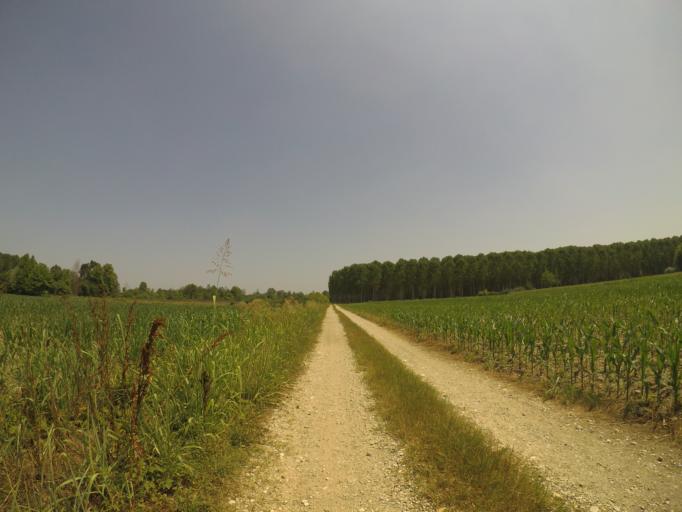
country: IT
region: Friuli Venezia Giulia
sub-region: Provincia di Udine
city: Bertiolo
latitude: 45.9267
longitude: 13.0517
